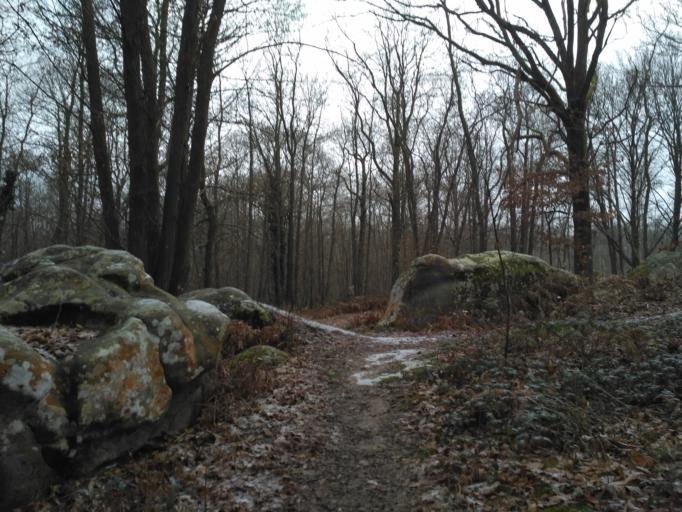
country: FR
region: Ile-de-France
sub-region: Departement de Seine-et-Marne
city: Vert-Saint-Denis
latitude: 48.5574
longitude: 2.6266
